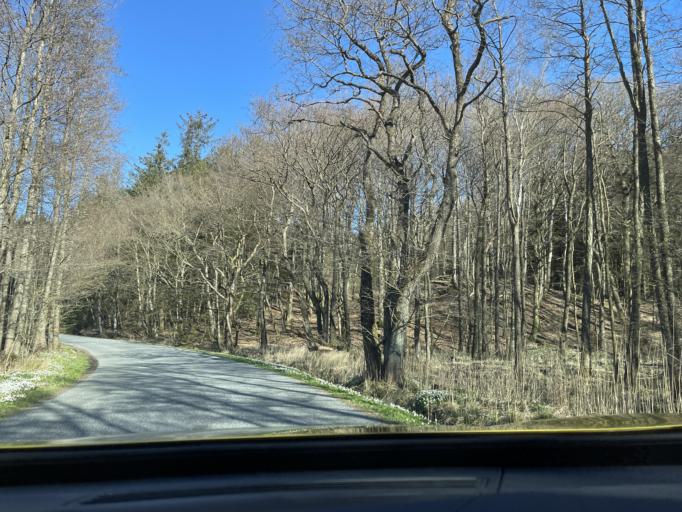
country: DK
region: Central Jutland
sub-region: Silkeborg Kommune
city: Kjellerup
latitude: 56.2464
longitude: 9.4712
